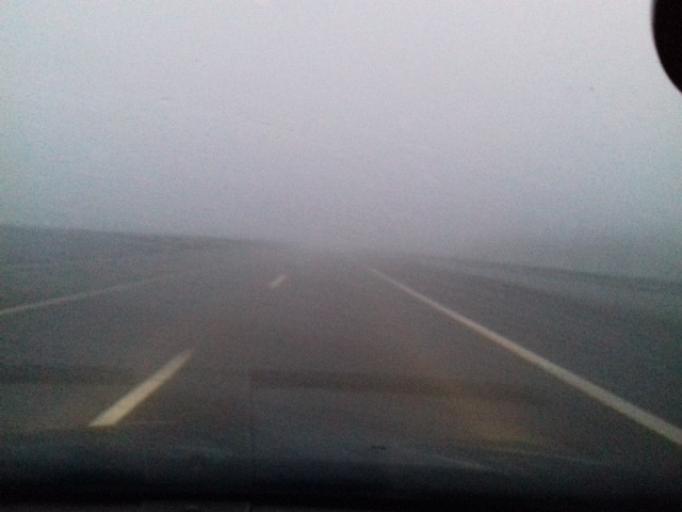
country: HU
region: Szabolcs-Szatmar-Bereg
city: Nagycserkesz
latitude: 47.9030
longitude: 21.5145
